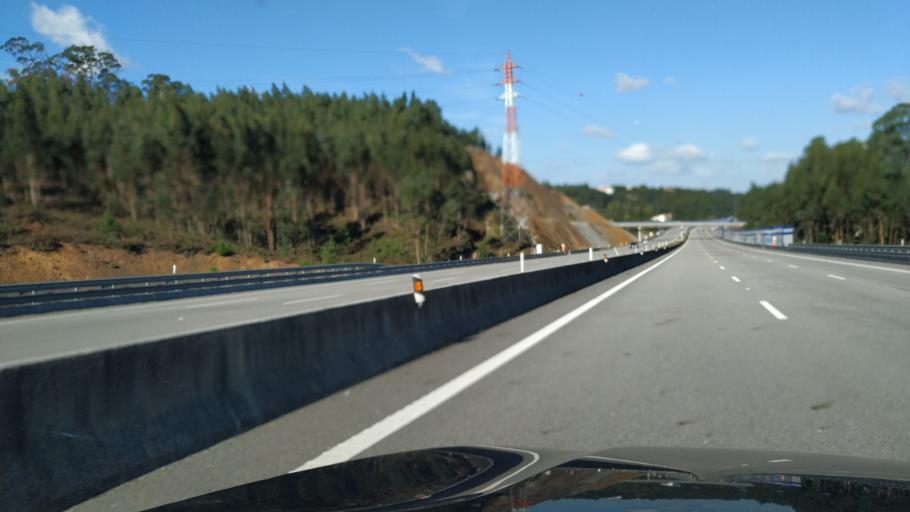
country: PT
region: Porto
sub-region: Vila Nova de Gaia
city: Olival
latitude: 41.0663
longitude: -8.5315
